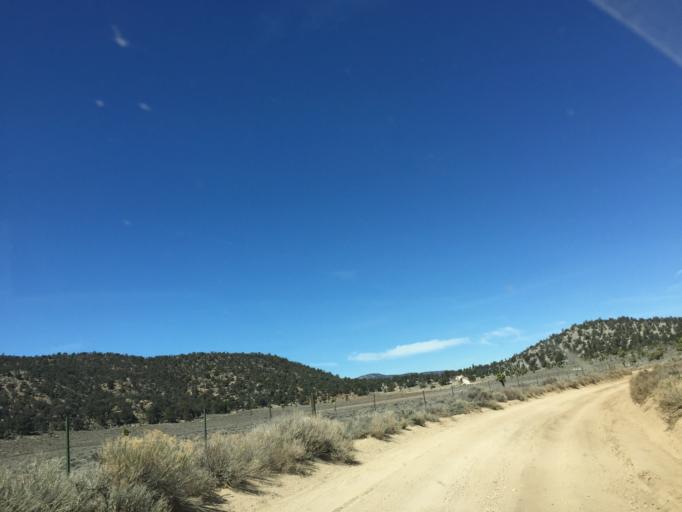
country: US
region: California
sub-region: San Bernardino County
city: Big Bear City
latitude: 34.2525
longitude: -116.7073
